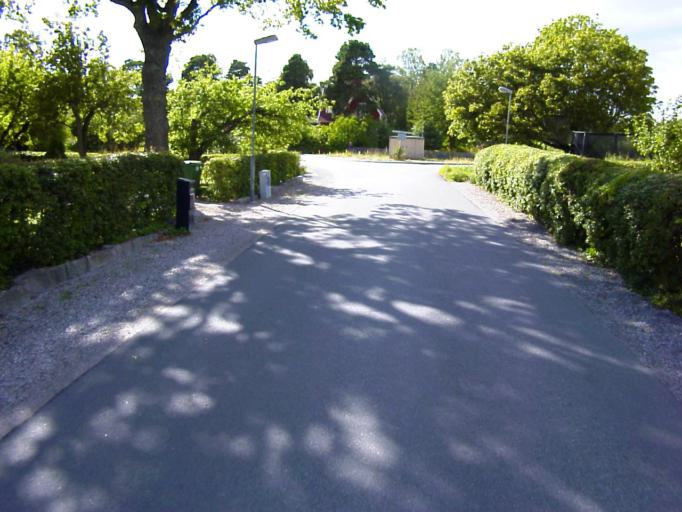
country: SE
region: Soedermanland
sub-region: Eskilstuna Kommun
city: Eskilstuna
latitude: 59.3725
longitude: 16.4930
